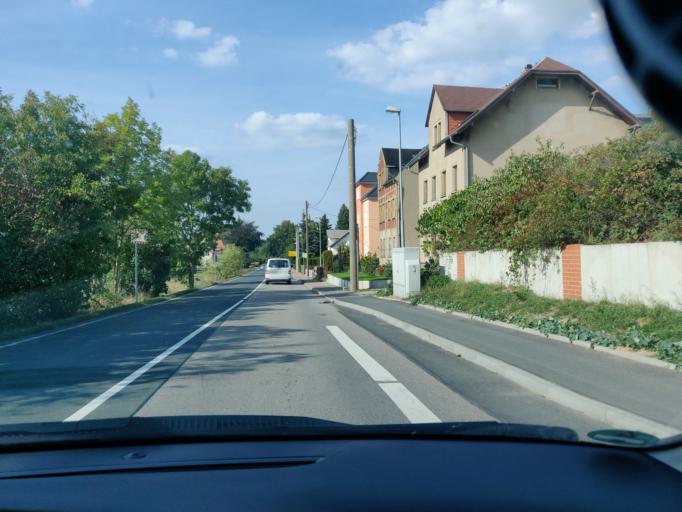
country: DE
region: Saxony
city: Erlau
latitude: 51.0070
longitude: 12.9475
